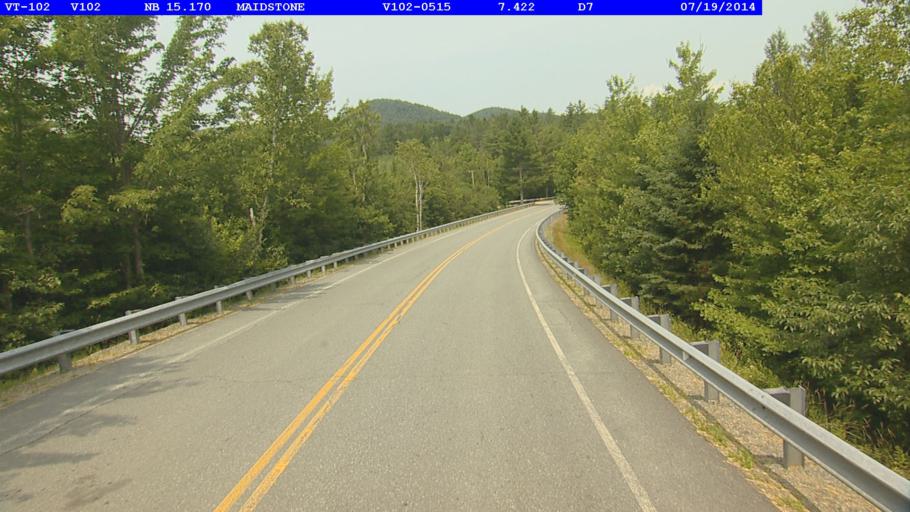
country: US
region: New Hampshire
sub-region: Coos County
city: Stratford
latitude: 44.6569
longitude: -71.5906
